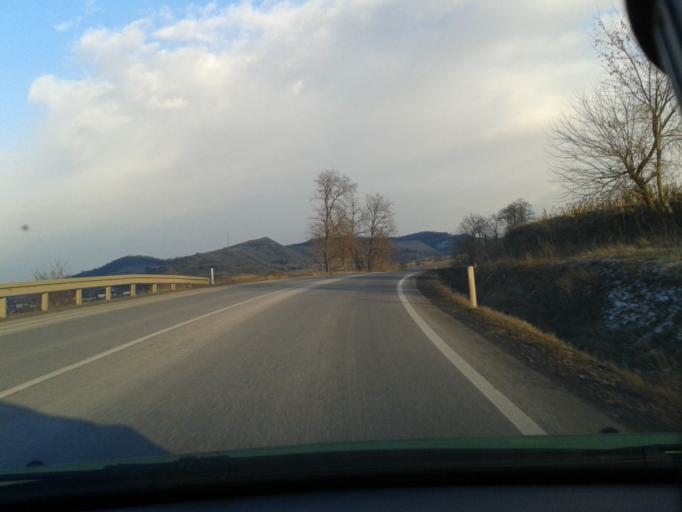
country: RO
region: Sibiu
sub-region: Comuna Tarnava
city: Tarnava
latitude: 46.1268
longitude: 24.2896
